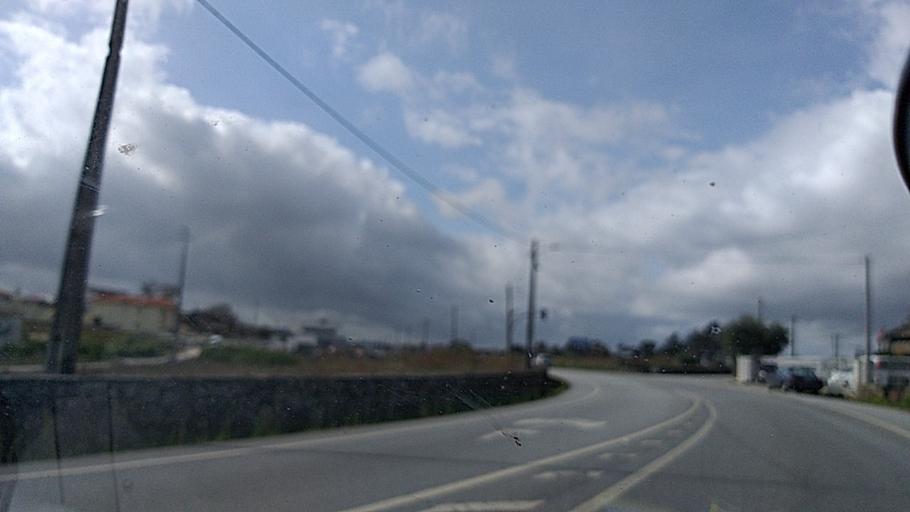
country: PT
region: Viseu
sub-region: Satao
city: Satao
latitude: 40.6694
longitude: -7.7105
